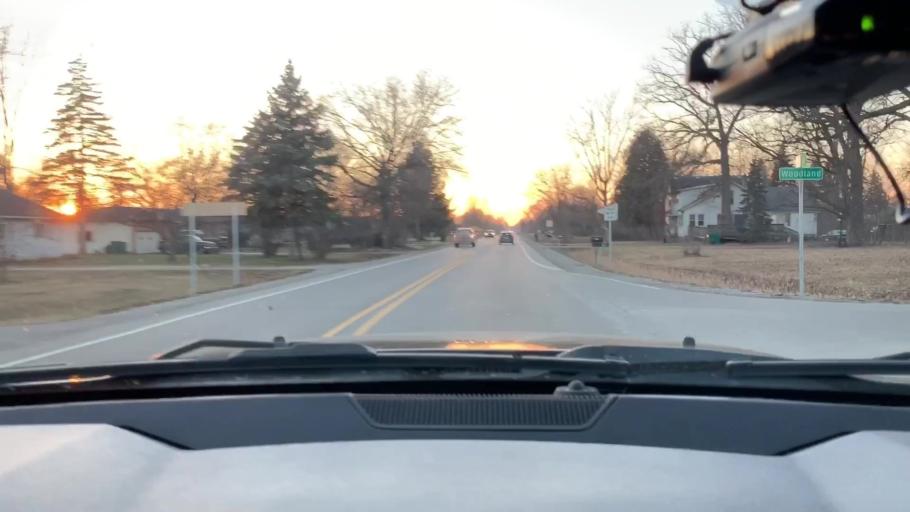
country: US
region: Michigan
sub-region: Wayne County
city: Flat Rock
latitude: 42.1237
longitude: -83.2775
